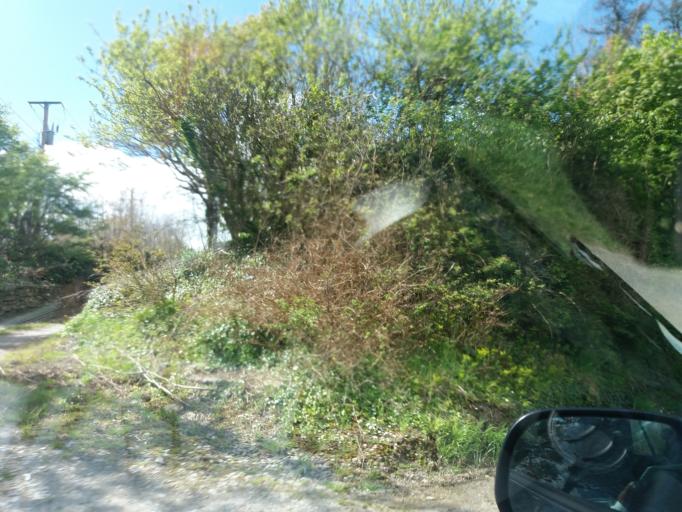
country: IE
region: Munster
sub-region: Waterford
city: Dunmore East
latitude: 52.2167
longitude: -6.9168
